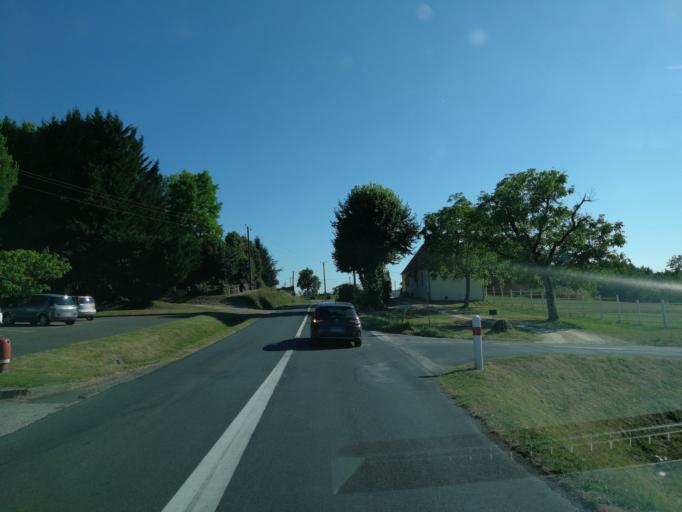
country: FR
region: Midi-Pyrenees
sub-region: Departement du Lot
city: Gourdon
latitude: 44.7205
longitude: 1.3676
